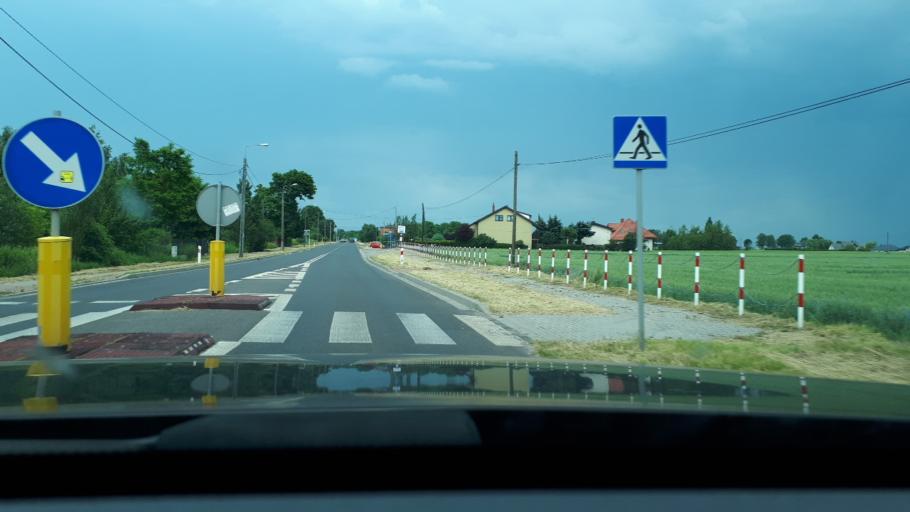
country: PL
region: Masovian Voivodeship
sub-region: Powiat warszawski zachodni
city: Kampinos
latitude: 52.2589
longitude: 20.5264
